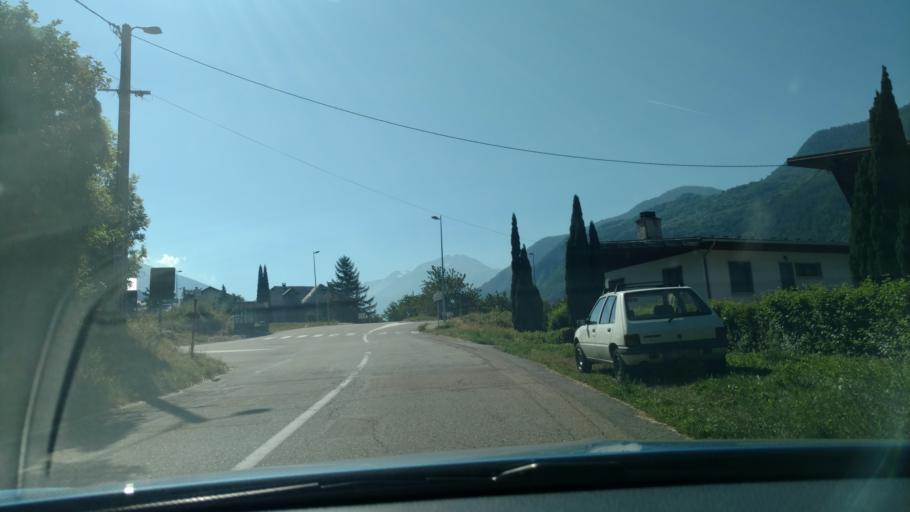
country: FR
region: Rhone-Alpes
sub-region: Departement de la Savoie
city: Villargondran
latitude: 45.2575
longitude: 6.3959
